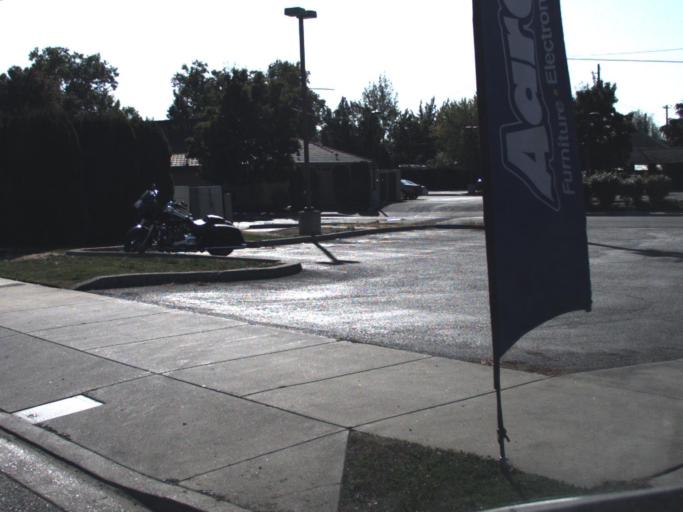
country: US
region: Washington
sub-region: Walla Walla County
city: Walla Walla
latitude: 46.0590
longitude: -118.3461
